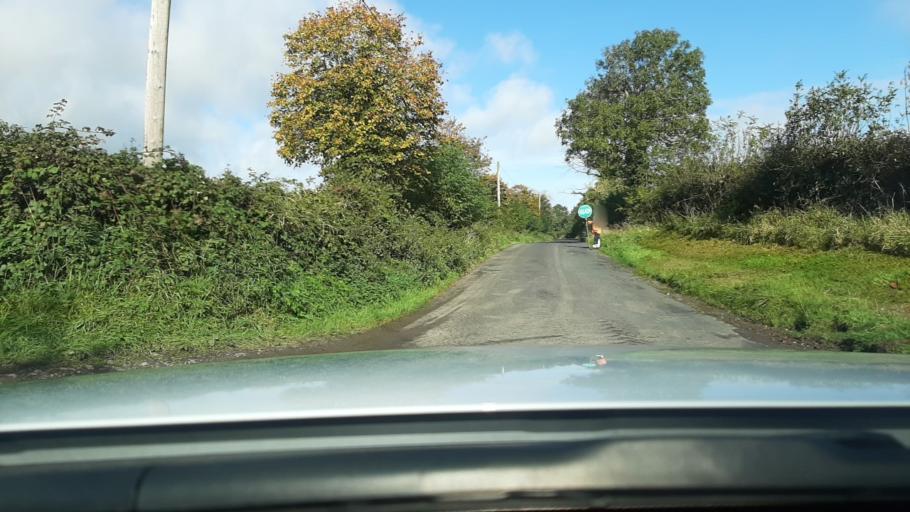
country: IE
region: Leinster
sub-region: Kildare
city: Kildare
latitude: 53.1708
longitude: -6.9208
